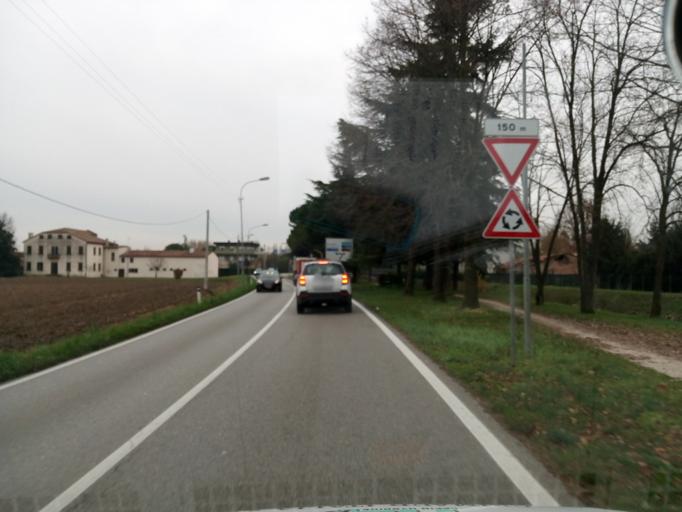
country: IT
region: Veneto
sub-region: Provincia di Padova
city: Vigonza
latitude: 45.4441
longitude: 11.9630
